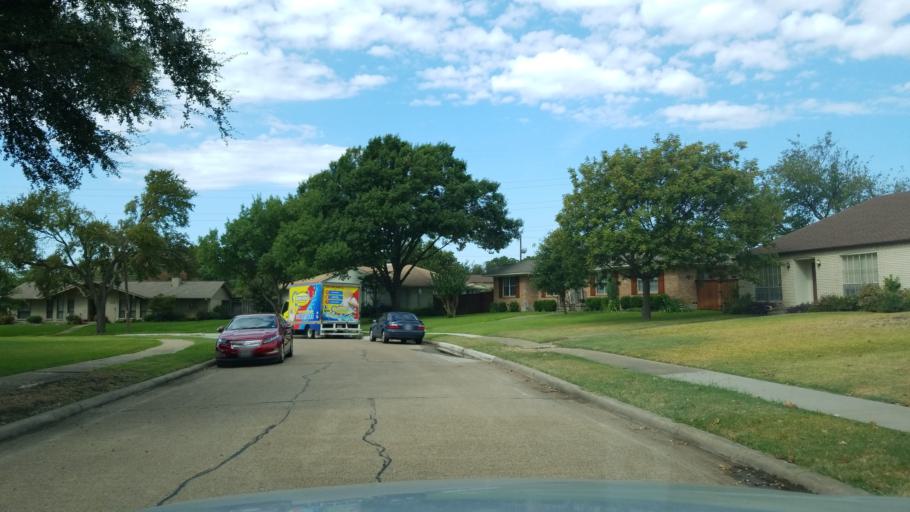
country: US
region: Texas
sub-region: Dallas County
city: Richardson
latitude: 32.9635
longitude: -96.7771
